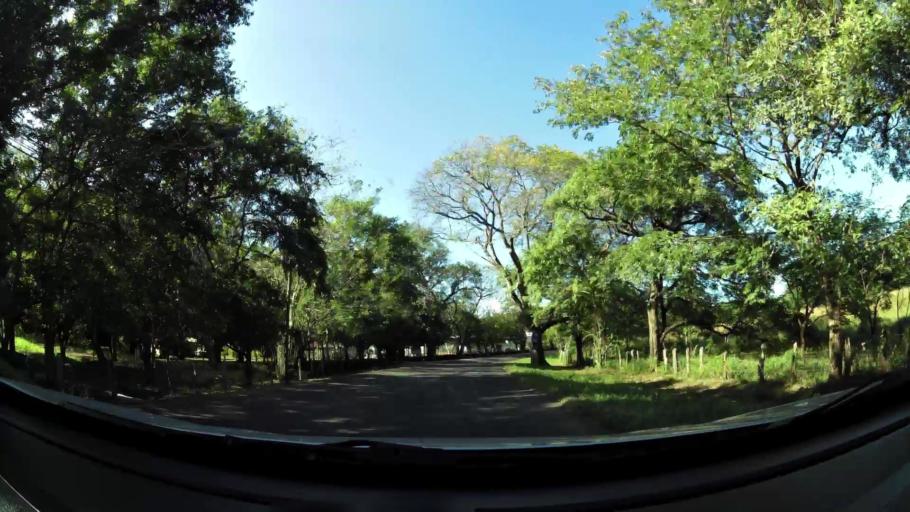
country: CR
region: Guanacaste
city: Sardinal
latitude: 10.5610
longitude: -85.5951
